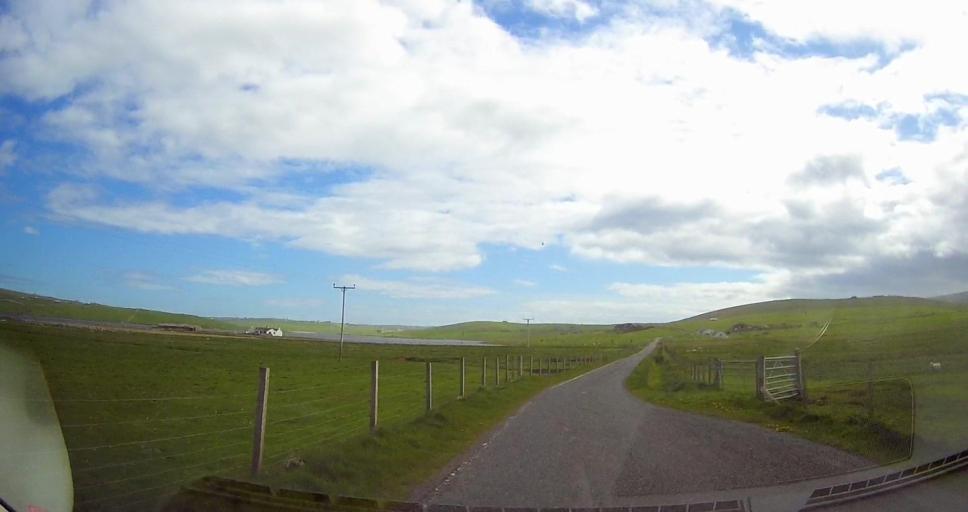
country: GB
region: Scotland
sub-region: Shetland Islands
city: Sandwick
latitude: 59.9379
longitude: -1.3461
